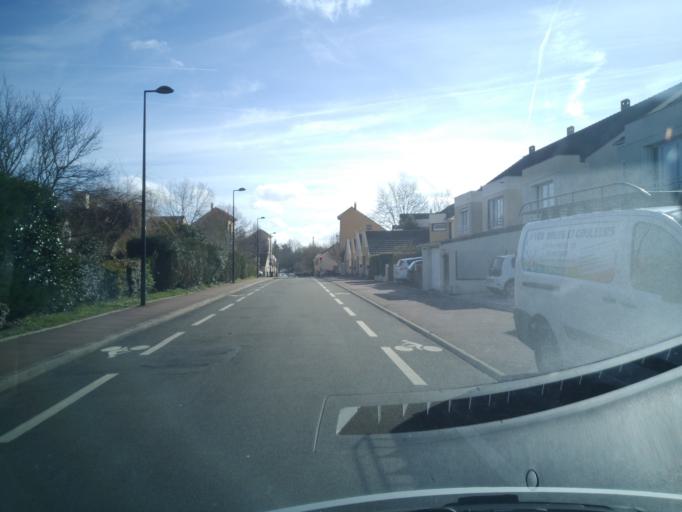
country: FR
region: Ile-de-France
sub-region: Departement des Yvelines
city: Voisins-le-Bretonneux
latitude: 48.7750
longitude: 2.0537
